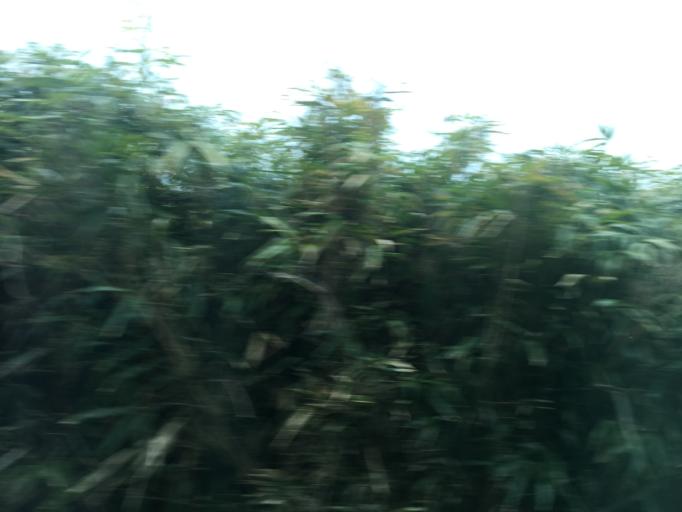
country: JP
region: Akita
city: Noshiromachi
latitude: 40.5875
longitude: 139.9118
